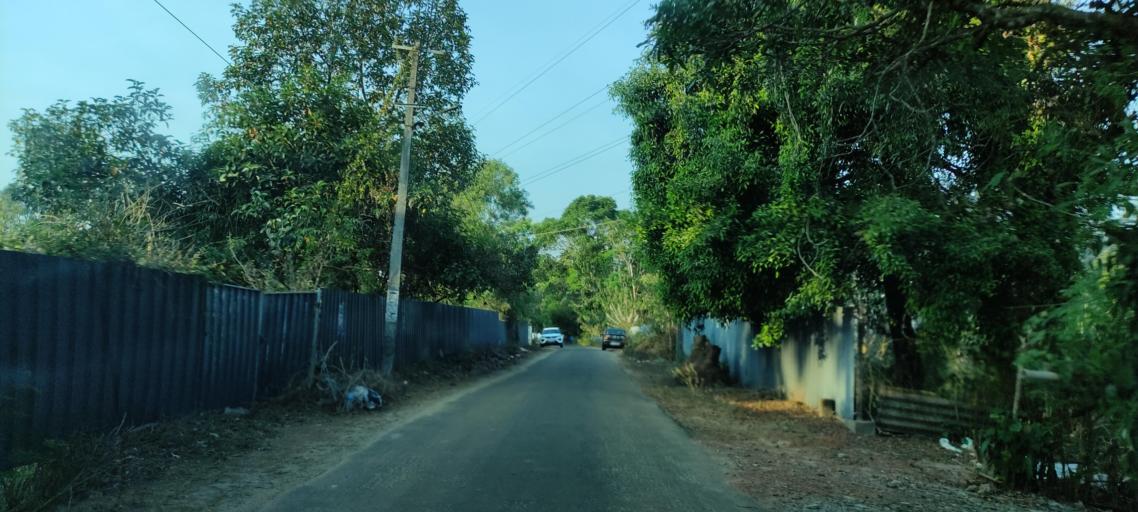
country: IN
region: Kerala
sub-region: Alappuzha
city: Vayalar
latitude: 9.7260
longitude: 76.3568
